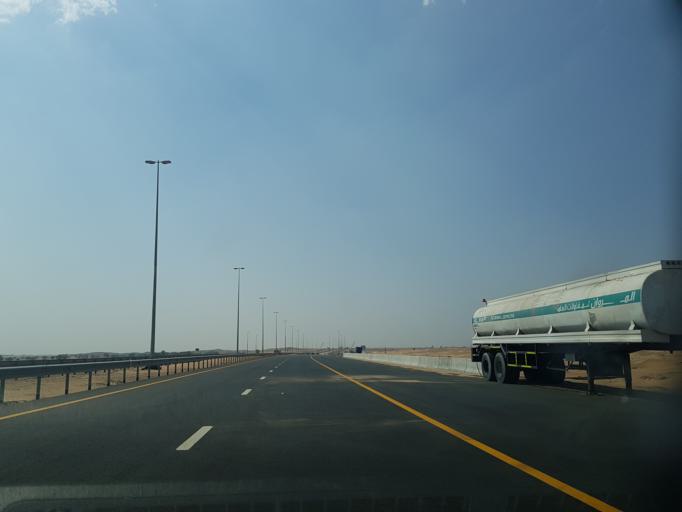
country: AE
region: Ash Shariqah
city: Adh Dhayd
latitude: 25.2616
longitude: 55.6739
